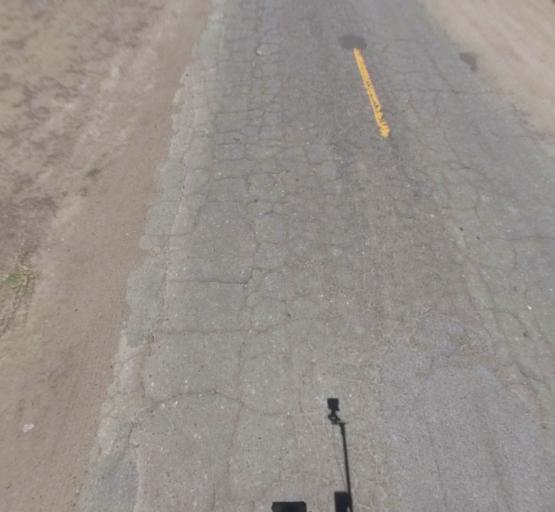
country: US
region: California
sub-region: Madera County
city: Chowchilla
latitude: 37.0762
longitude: -120.2855
